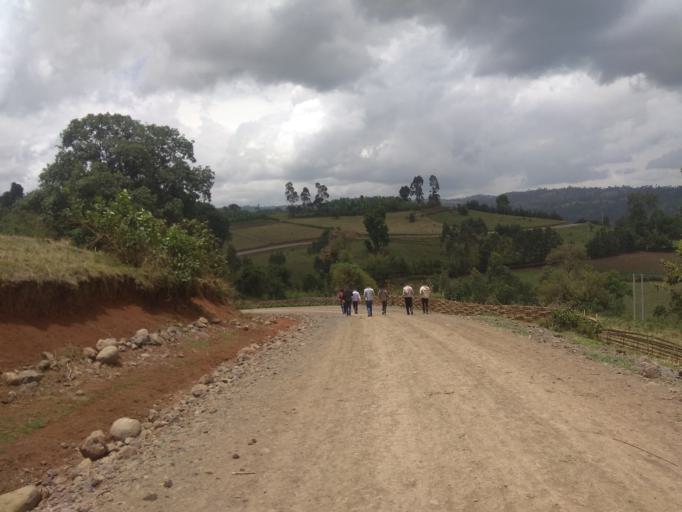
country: ET
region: Oromiya
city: Guder
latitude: 8.7499
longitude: 37.6295
